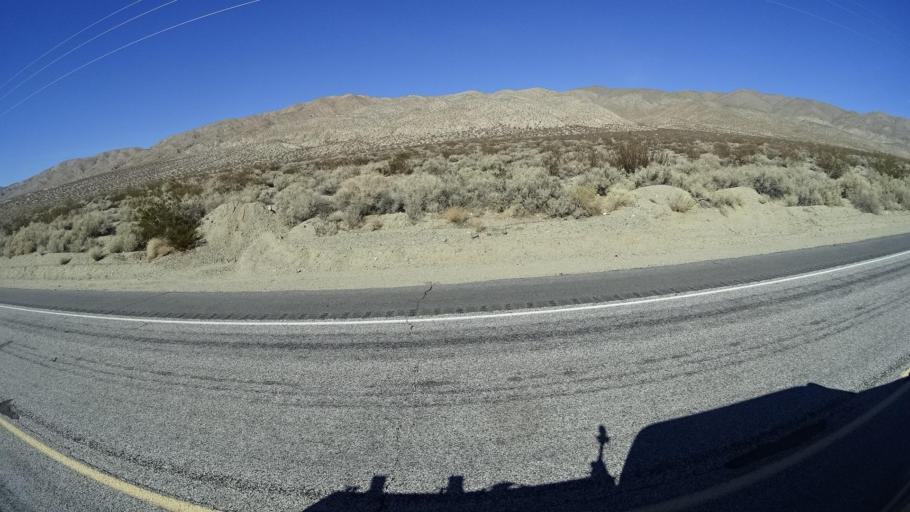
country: US
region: California
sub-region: Kern County
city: California City
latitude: 35.3716
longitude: -117.8776
